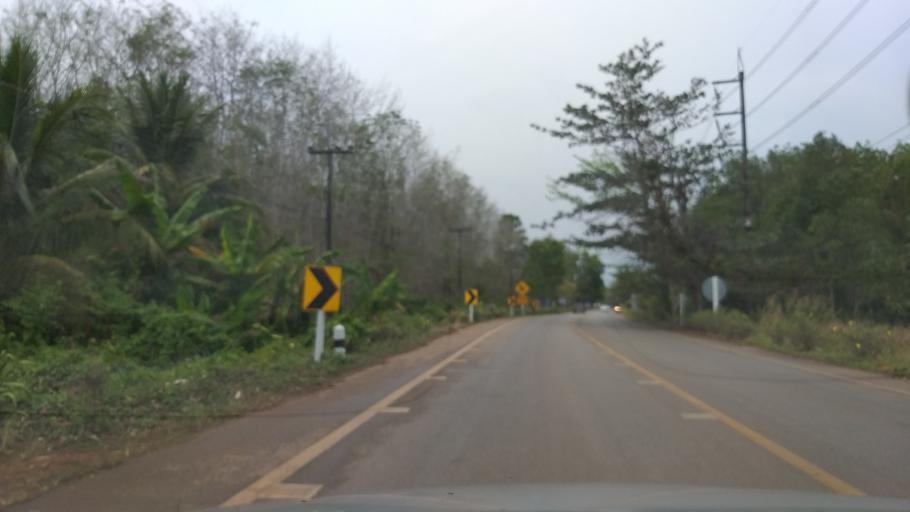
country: TH
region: Trat
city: Laem Ngop
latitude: 12.2266
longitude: 102.3065
